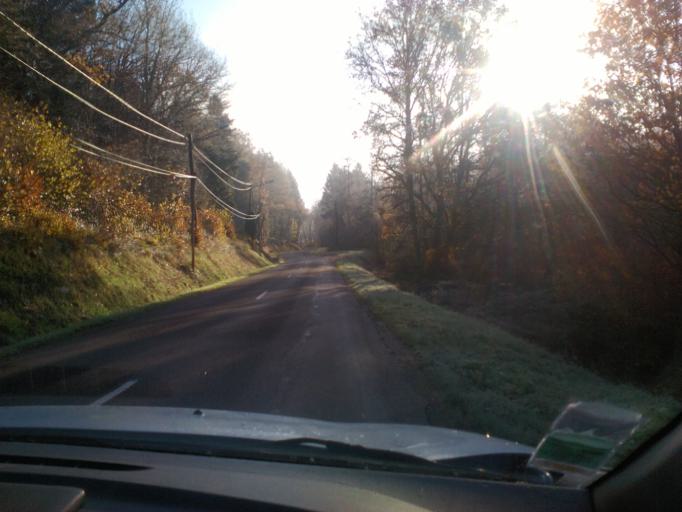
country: FR
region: Lorraine
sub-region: Departement des Vosges
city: Uzemain
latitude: 48.0632
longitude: 6.3318
